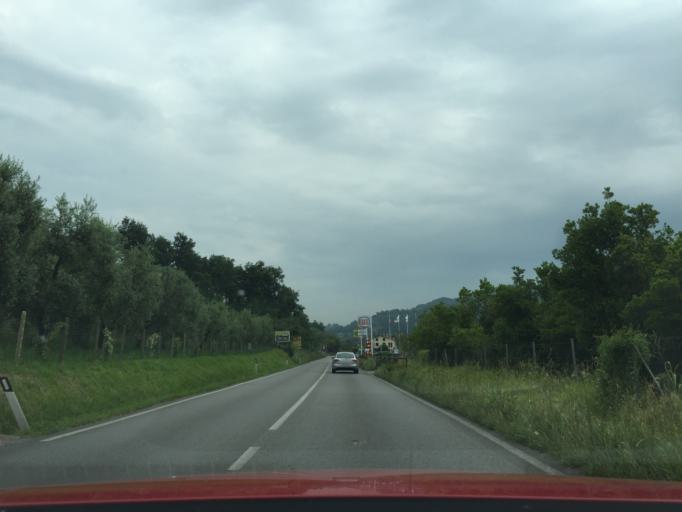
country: IT
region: Tuscany
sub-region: Provincia di Pistoia
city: Pieve a Nievole
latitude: 43.8881
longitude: 10.8132
